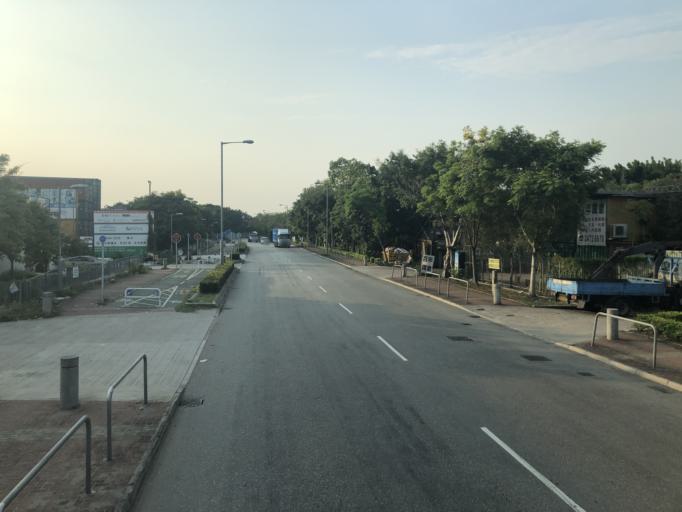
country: HK
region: Yuen Long
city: Yuen Long Kau Hui
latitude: 22.4568
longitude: 113.9917
